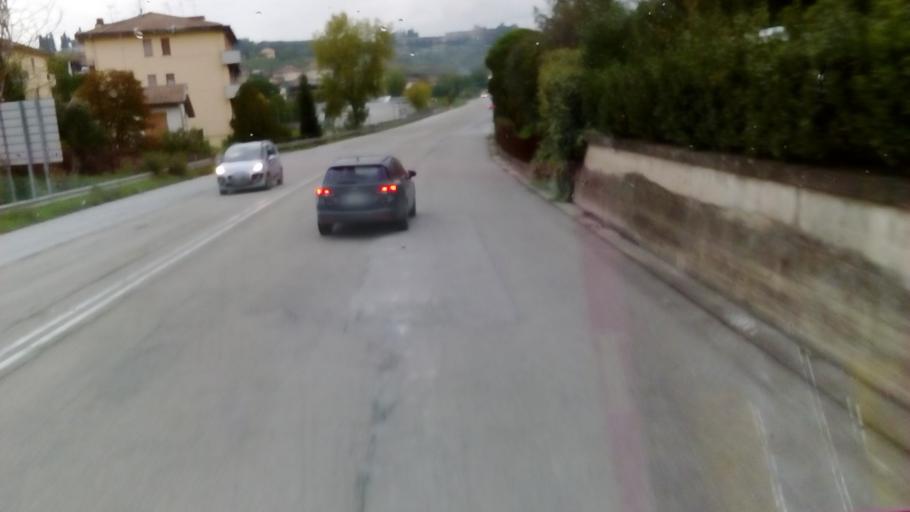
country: IT
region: Tuscany
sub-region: Province of Florence
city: Castelfiorentino
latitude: 43.6003
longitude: 10.9749
